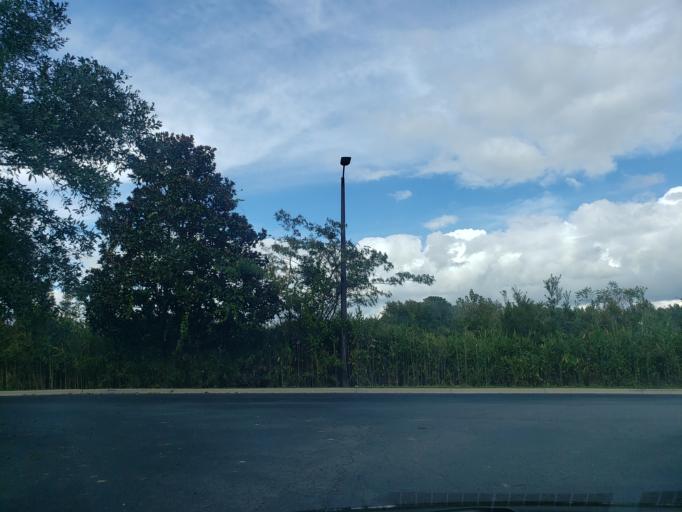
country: US
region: Georgia
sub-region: Chatham County
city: Georgetown
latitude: 32.0052
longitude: -81.2755
